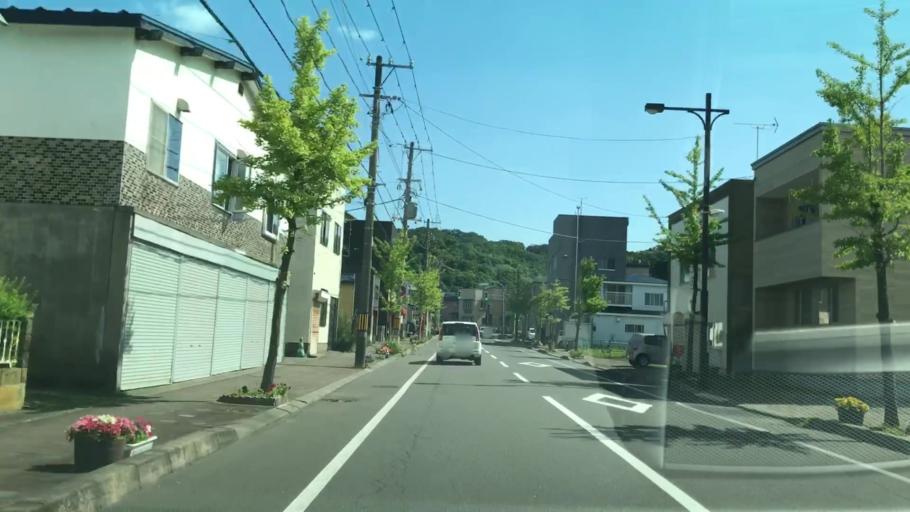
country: JP
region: Hokkaido
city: Muroran
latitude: 42.3139
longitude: 140.9909
